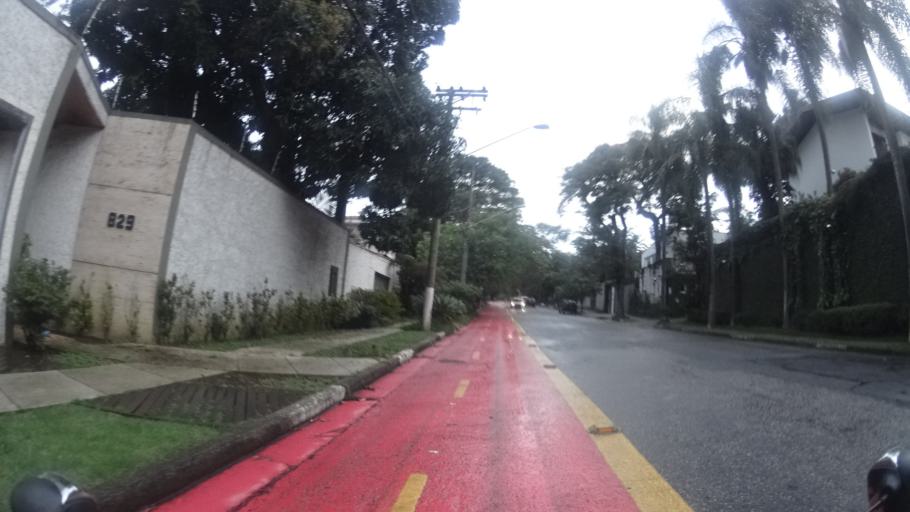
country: BR
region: Sao Paulo
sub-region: Sao Paulo
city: Sao Paulo
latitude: -23.5818
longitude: -46.7041
